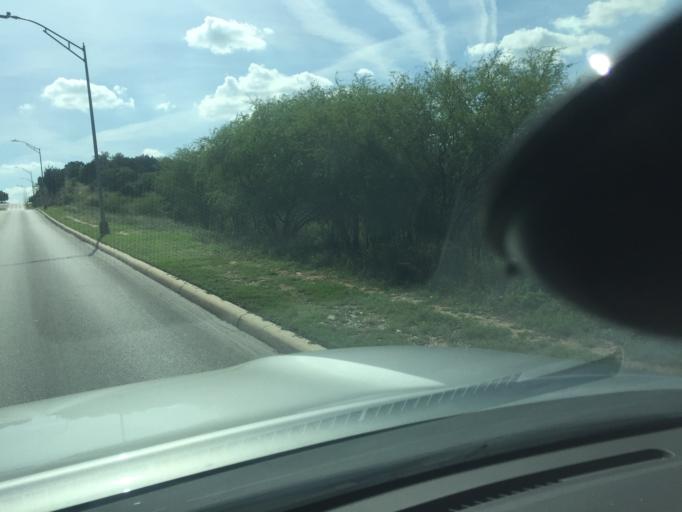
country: US
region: Texas
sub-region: Bexar County
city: Hollywood Park
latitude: 29.6429
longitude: -98.4838
